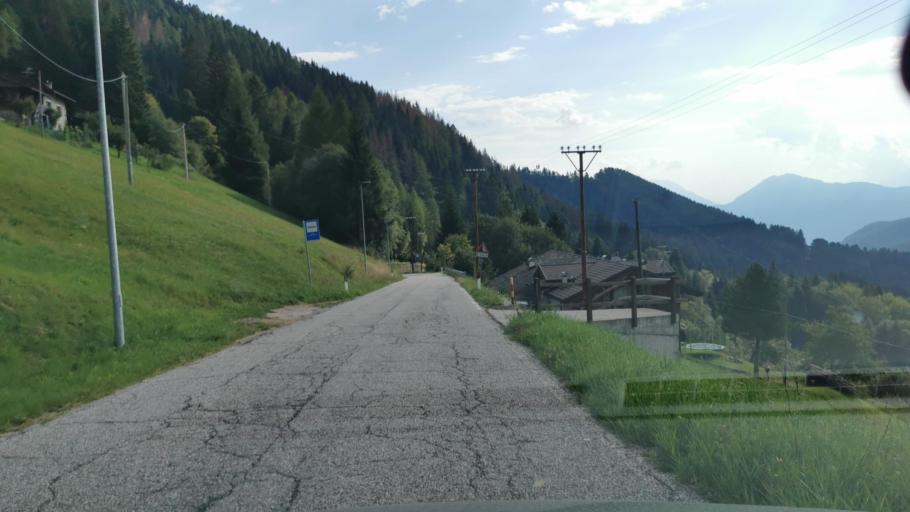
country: IT
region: Trentino-Alto Adige
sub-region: Provincia di Trento
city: Palu del Fersina
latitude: 46.1223
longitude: 11.3395
